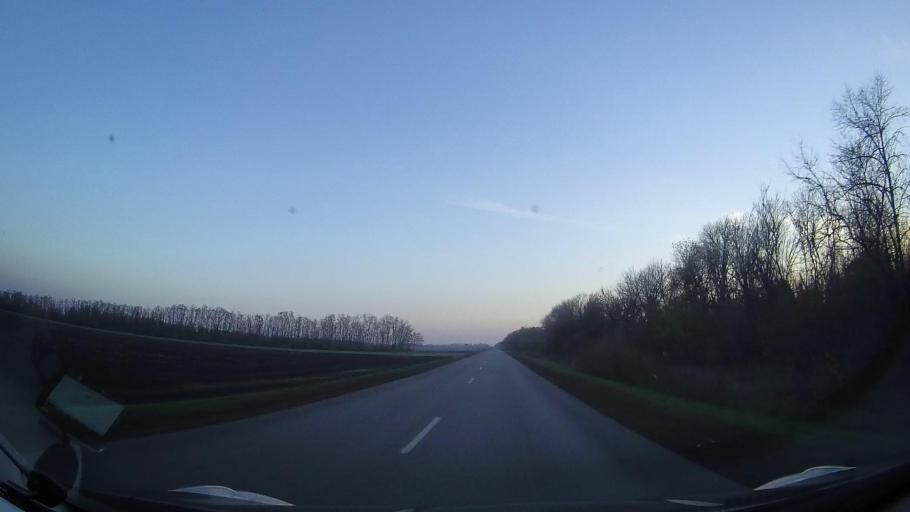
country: RU
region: Rostov
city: Zernograd
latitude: 47.0114
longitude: 40.3916
